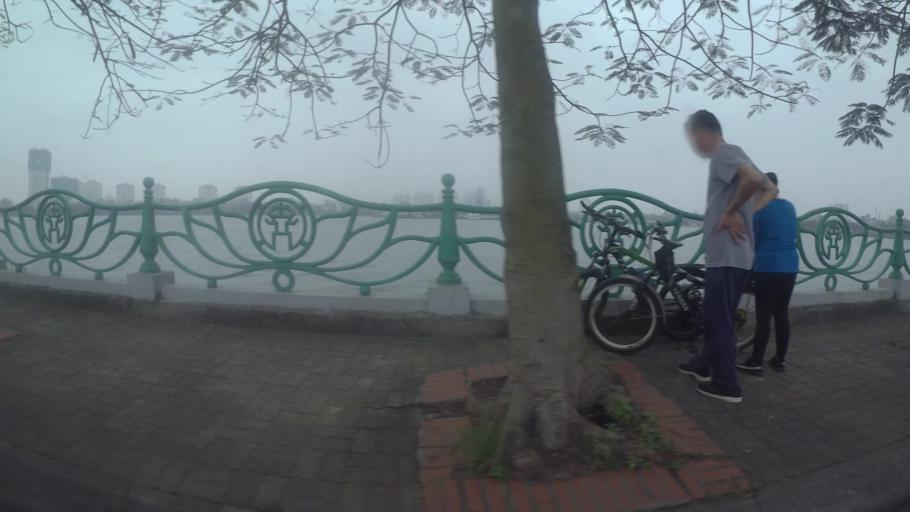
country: VN
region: Ha Noi
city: Tay Ho
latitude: 21.0683
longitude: 105.8193
